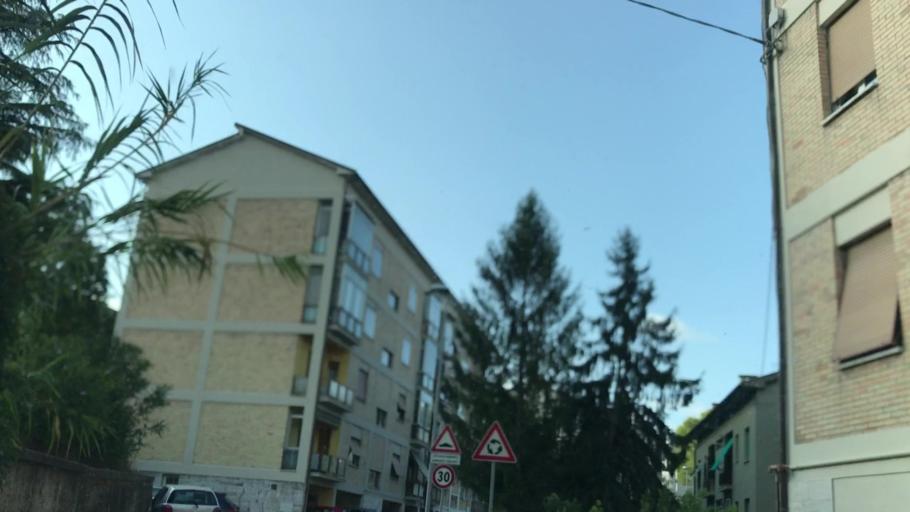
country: IT
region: The Marches
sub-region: Provincia di Ancona
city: Le Grazie di Ancona
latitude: 43.5942
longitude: 13.5169
